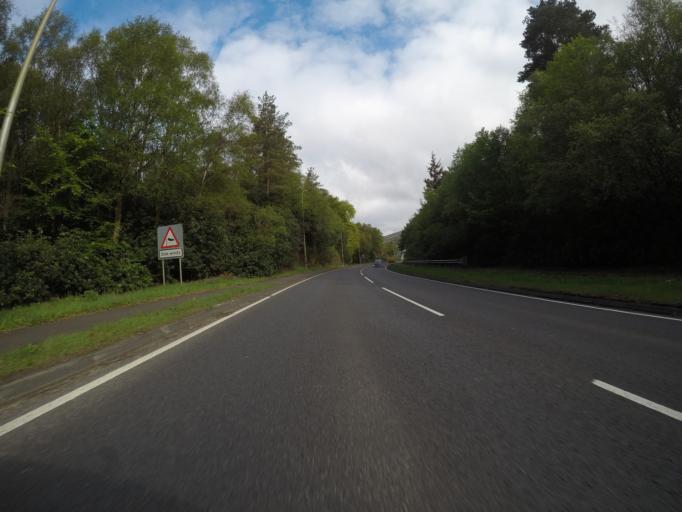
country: GB
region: Scotland
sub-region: Highland
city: Fort William
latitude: 56.6865
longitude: -5.1817
